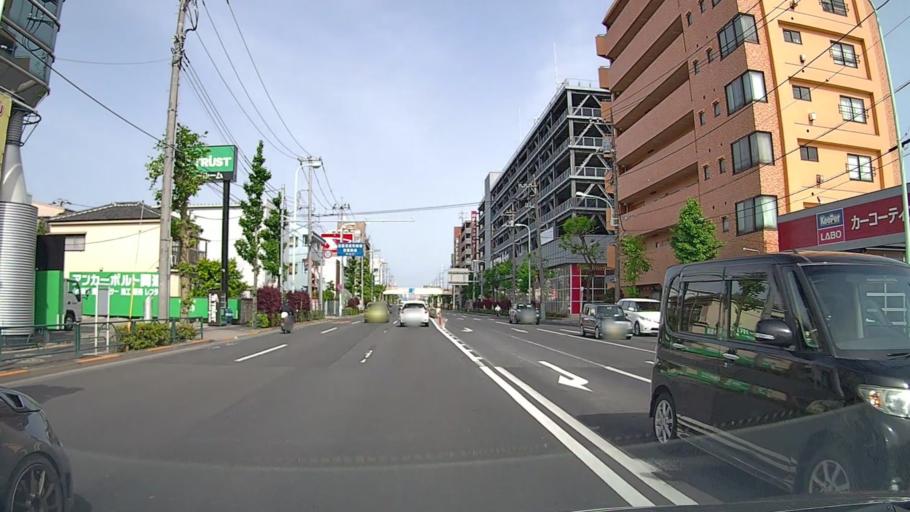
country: JP
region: Saitama
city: Kawaguchi
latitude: 35.7787
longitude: 139.7511
